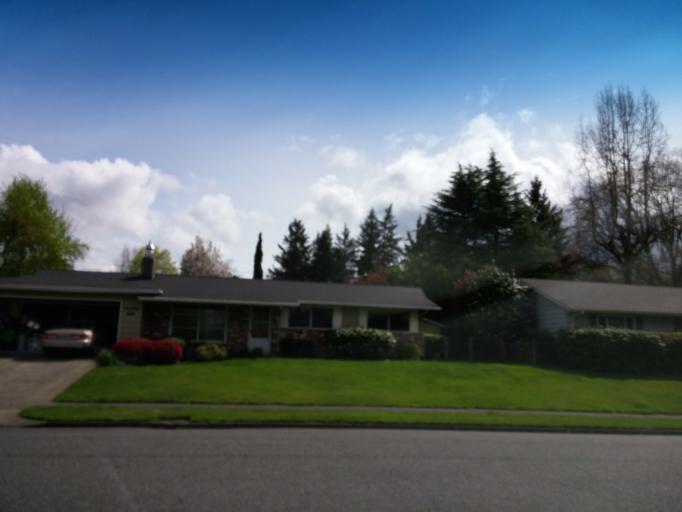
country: US
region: Oregon
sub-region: Washington County
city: Cedar Hills
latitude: 45.5083
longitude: -122.8022
